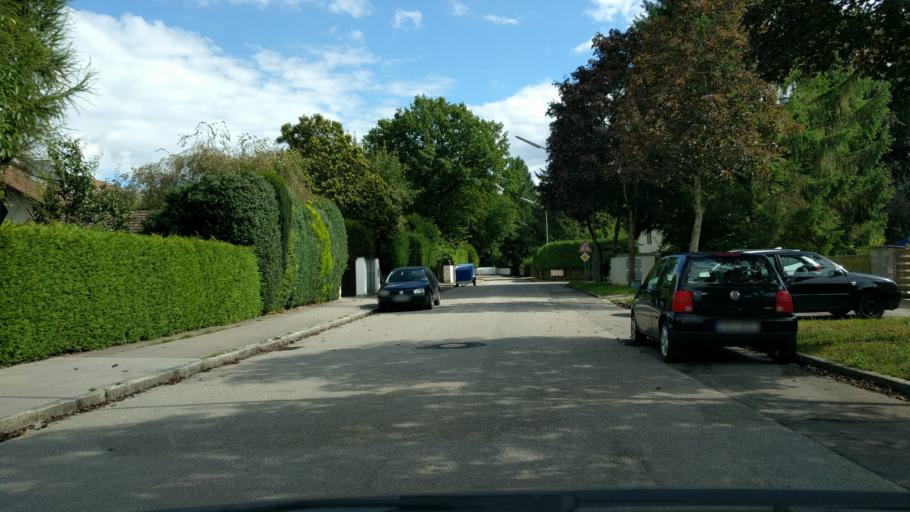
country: DE
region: Bavaria
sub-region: Upper Bavaria
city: Grunwald
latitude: 48.0404
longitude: 11.5383
